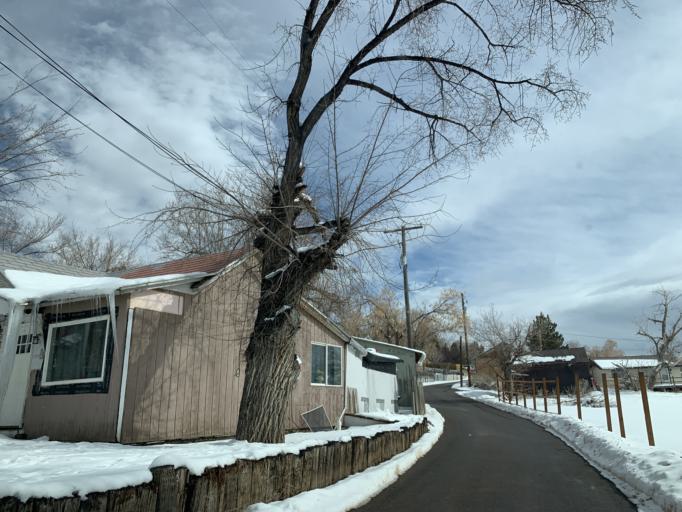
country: US
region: Utah
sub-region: Utah County
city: Genola
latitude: 39.9559
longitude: -112.1226
